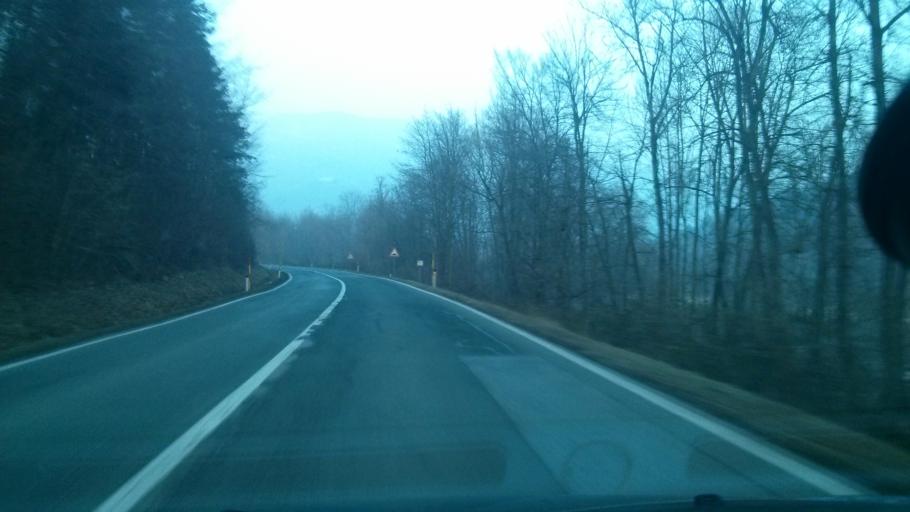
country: SI
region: Moravce
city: Moravce
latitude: 46.0953
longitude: 14.7701
